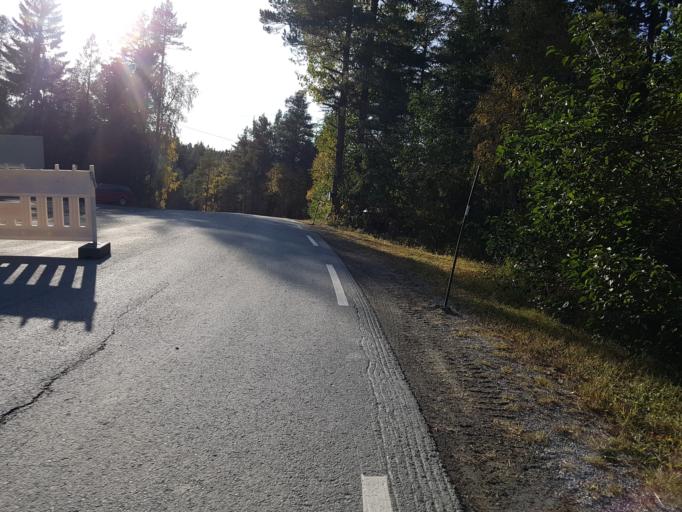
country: NO
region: Sor-Trondelag
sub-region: Klaebu
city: Klaebu
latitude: 63.3401
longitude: 10.5793
